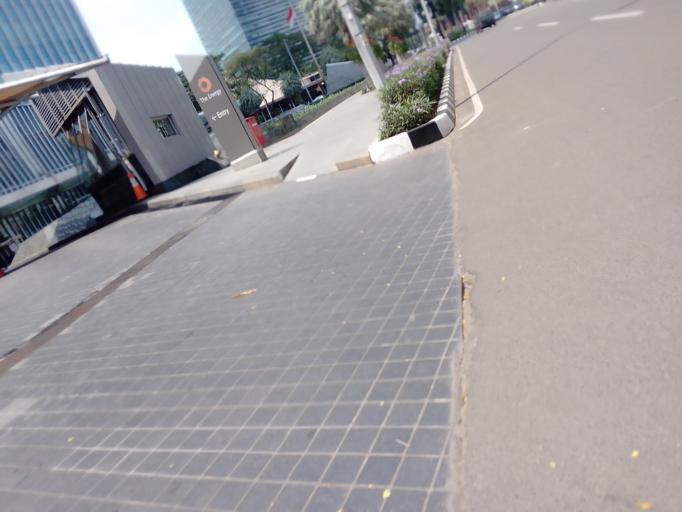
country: ID
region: Jakarta Raya
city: Jakarta
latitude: -6.2258
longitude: 106.8058
